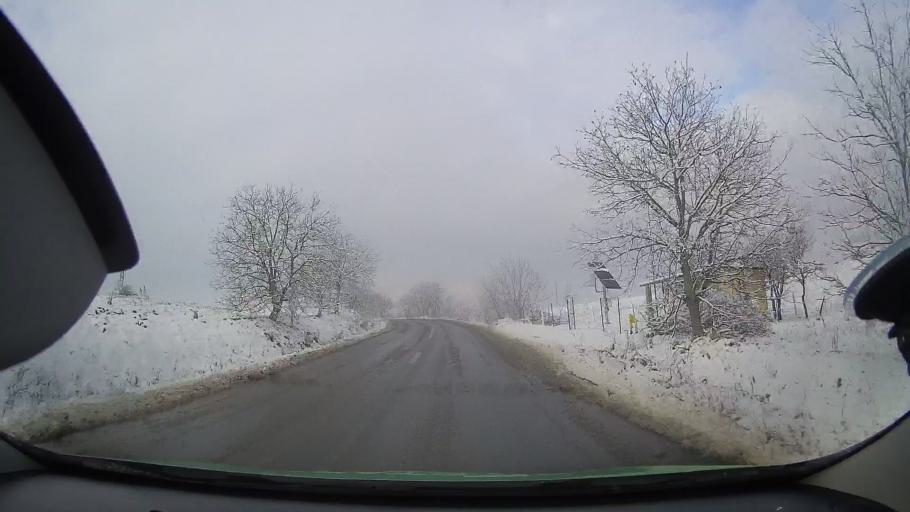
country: RO
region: Mures
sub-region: Comuna Atintis
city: Atintis
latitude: 46.4383
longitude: 24.0933
